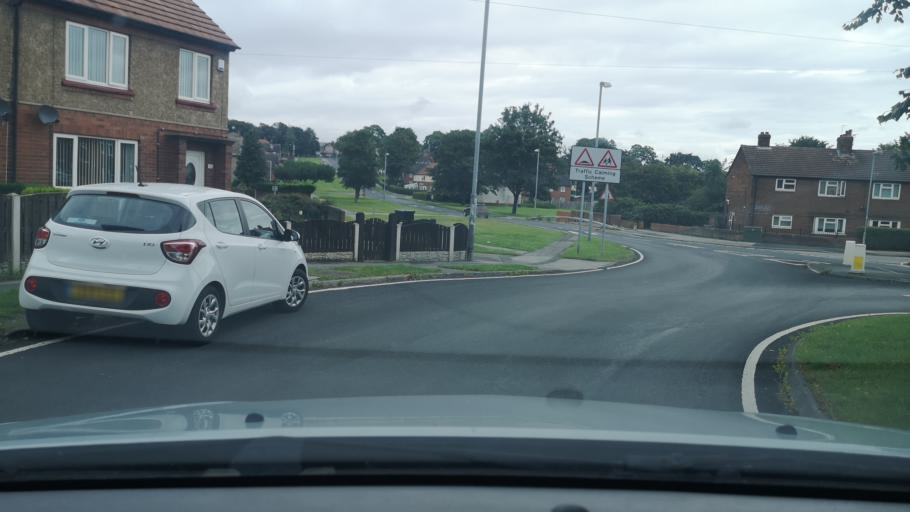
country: GB
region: England
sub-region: City and Borough of Wakefield
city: Wakefield
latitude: 53.6836
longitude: -1.5265
